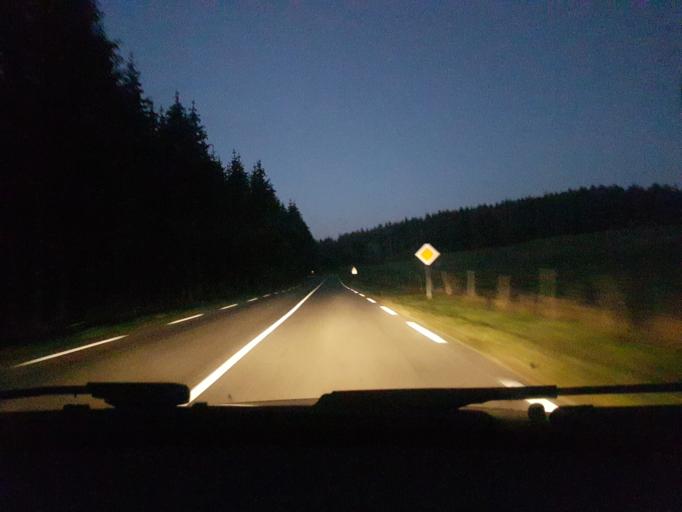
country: CH
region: Neuchatel
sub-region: Le Locle District
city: Les Brenets
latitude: 47.1129
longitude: 6.6932
